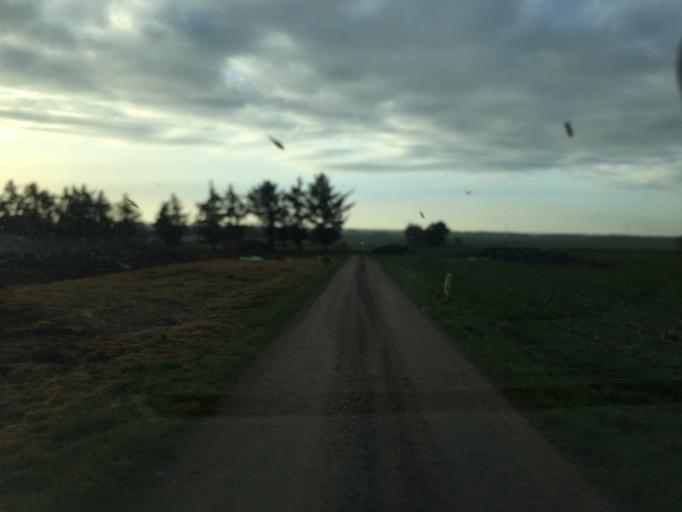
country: DK
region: South Denmark
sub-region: Tonder Kommune
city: Logumkloster
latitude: 55.1119
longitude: 8.8652
